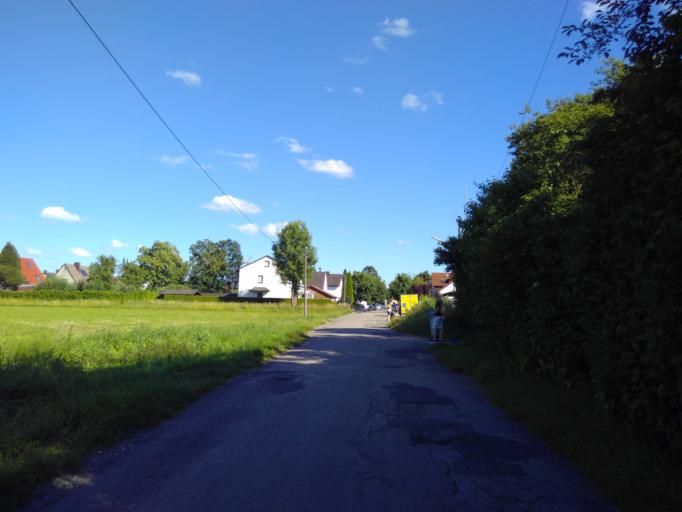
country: DE
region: Bavaria
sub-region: Upper Bavaria
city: Puchheim
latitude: 48.1700
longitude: 11.3413
